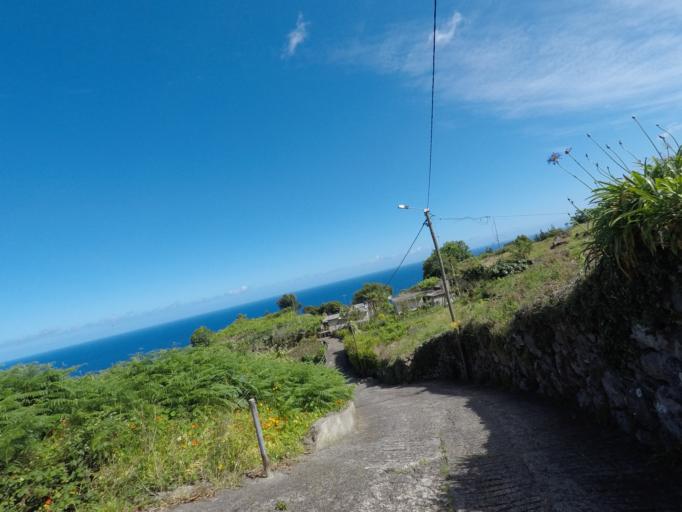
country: PT
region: Madeira
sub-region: Santana
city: Santana
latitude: 32.8244
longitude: -16.9491
